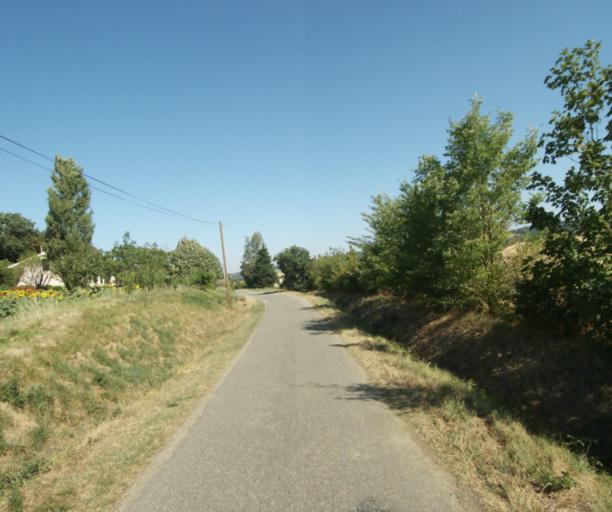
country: FR
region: Midi-Pyrenees
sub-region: Departement de la Haute-Garonne
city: Saint-Felix-Lauragais
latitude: 43.4977
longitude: 1.9269
